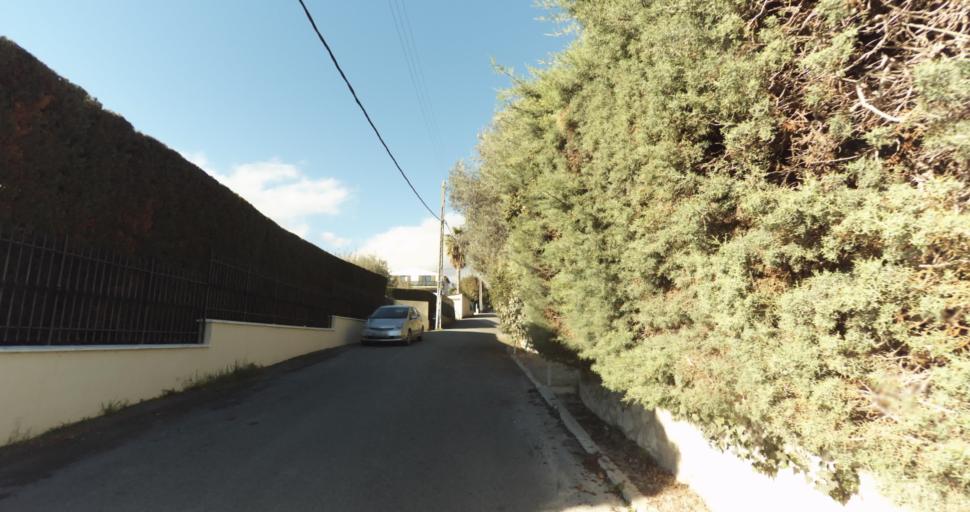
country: FR
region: Provence-Alpes-Cote d'Azur
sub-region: Departement des Alpes-Maritimes
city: Saint-Paul-de-Vence
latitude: 43.7026
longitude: 7.1348
